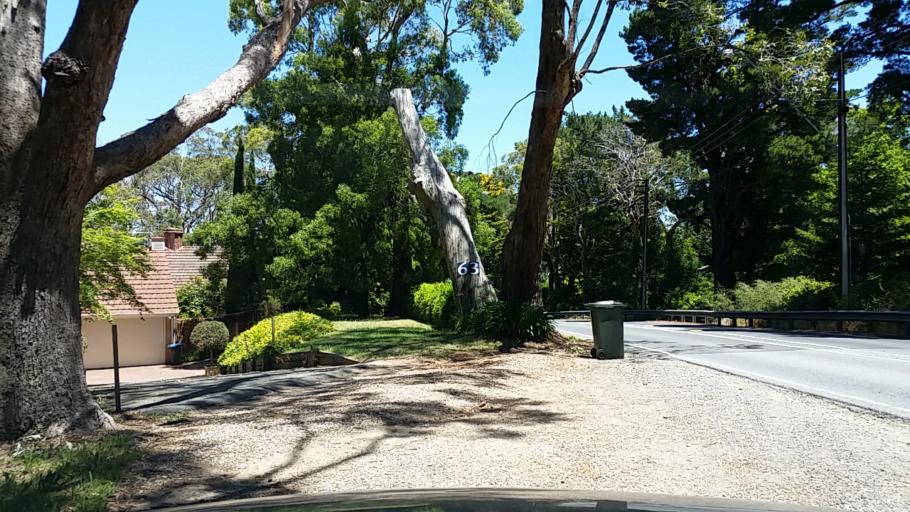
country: AU
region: South Australia
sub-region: Adelaide Hills
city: Crafers
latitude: -35.0062
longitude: 138.6988
